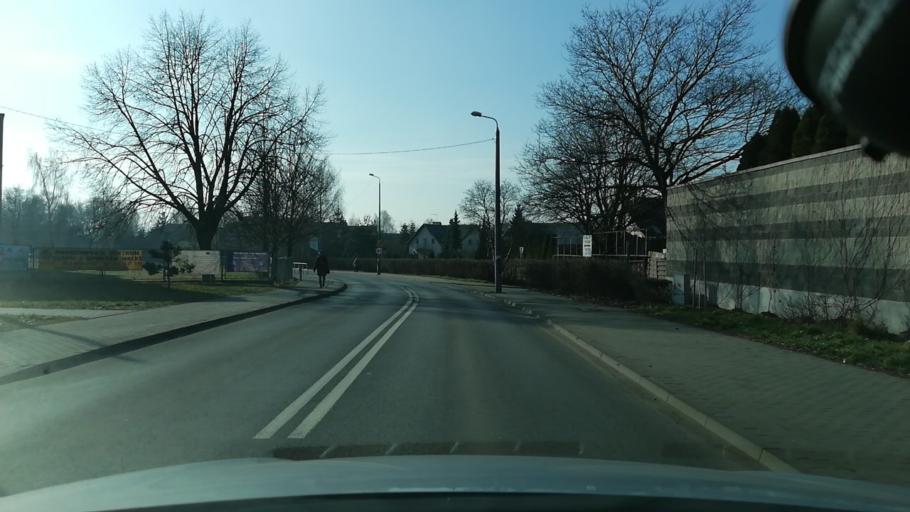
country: PL
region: Silesian Voivodeship
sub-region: Swietochlowice
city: Swietochlowice
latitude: 50.2700
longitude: 18.9314
